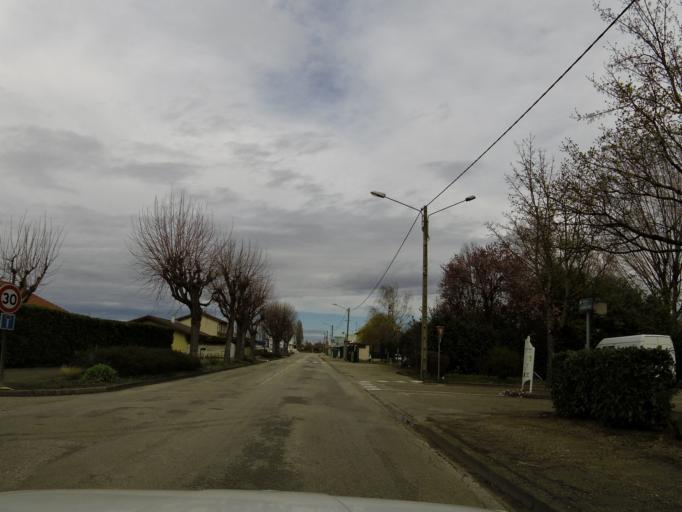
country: FR
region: Rhone-Alpes
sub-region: Departement de l'Ain
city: Amberieu-en-Bugey
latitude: 45.9622
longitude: 5.3359
